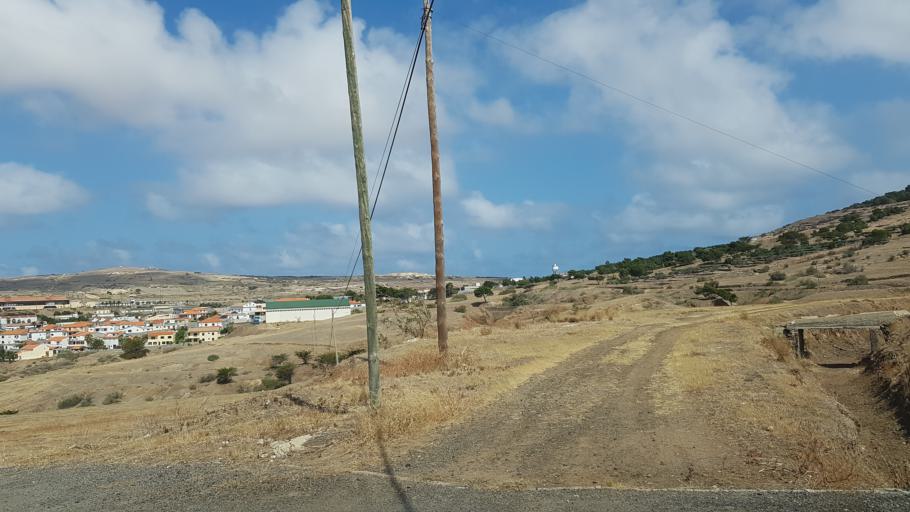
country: PT
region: Madeira
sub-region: Porto Santo
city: Vila de Porto Santo
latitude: 33.0694
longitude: -16.3339
